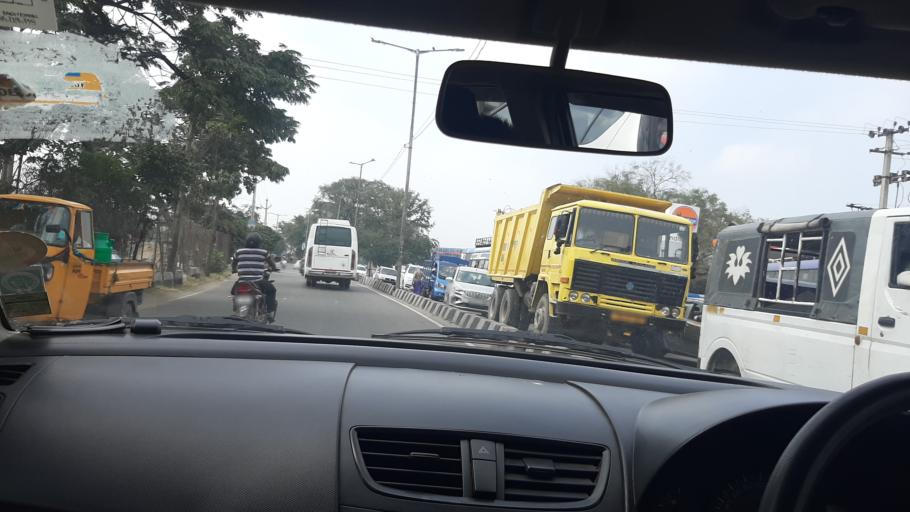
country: IN
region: Telangana
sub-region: Rangareddi
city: Lal Bahadur Nagar
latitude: 17.3427
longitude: 78.5458
